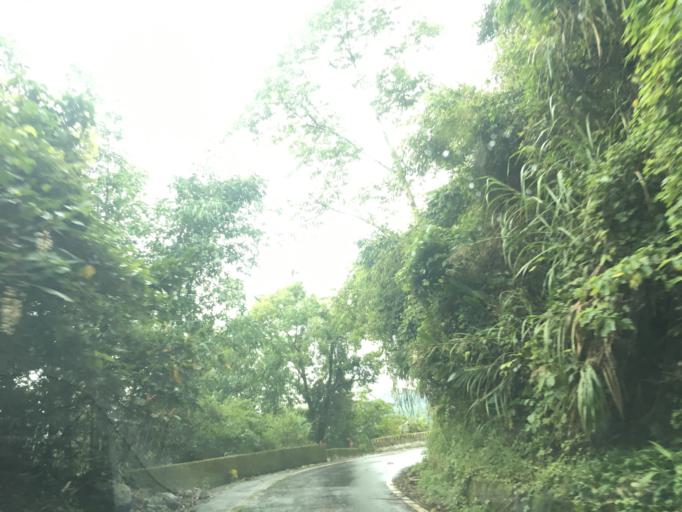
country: TW
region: Taiwan
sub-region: Yunlin
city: Douliu
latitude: 23.5610
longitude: 120.6538
